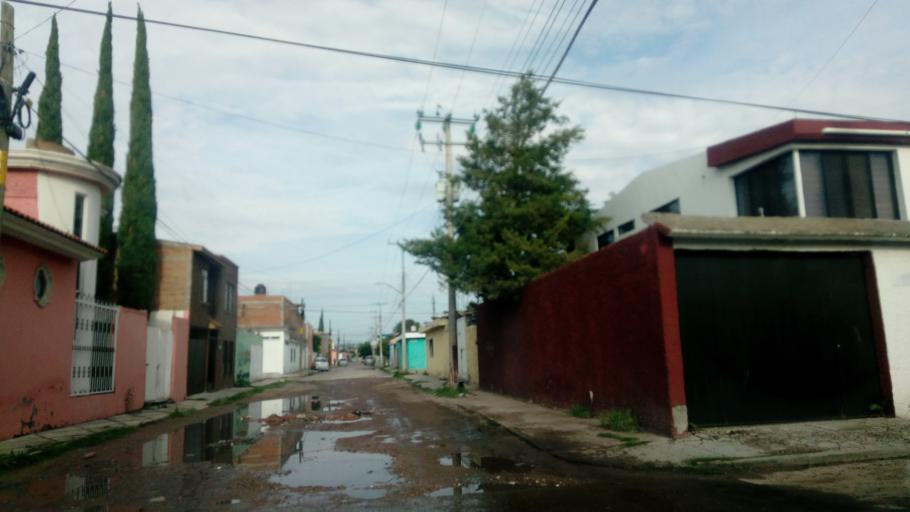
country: MX
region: Durango
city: Victoria de Durango
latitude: 24.0159
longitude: -104.6501
